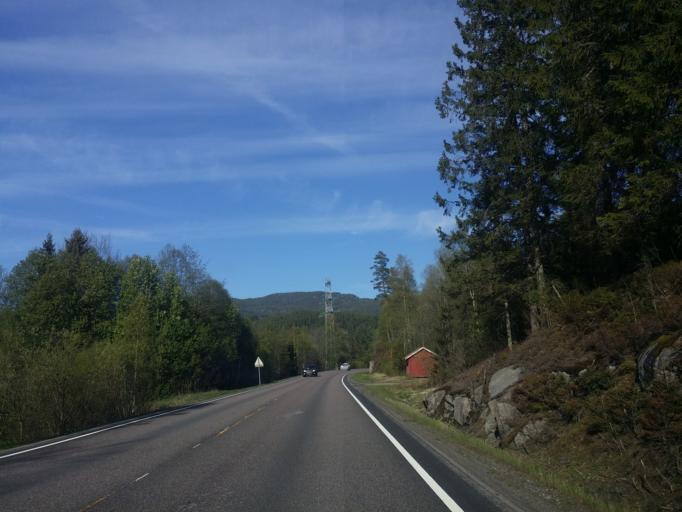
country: NO
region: Telemark
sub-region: Hjartdal
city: Sauland
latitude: 59.6098
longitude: 8.9790
